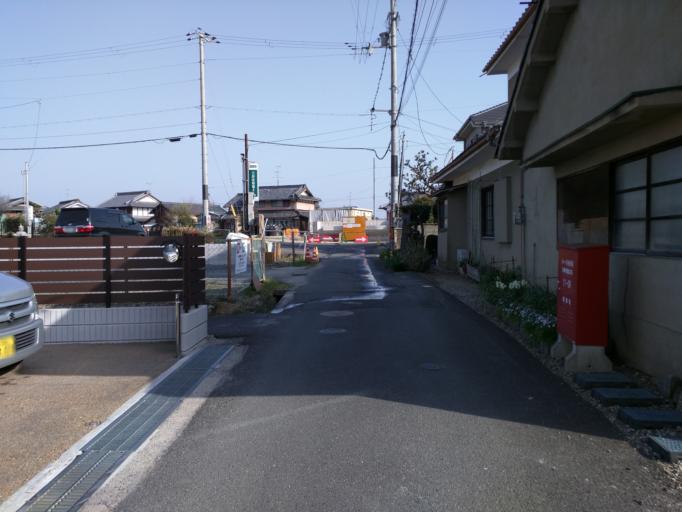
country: JP
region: Kyoto
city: Tanabe
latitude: 34.7817
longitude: 135.7953
